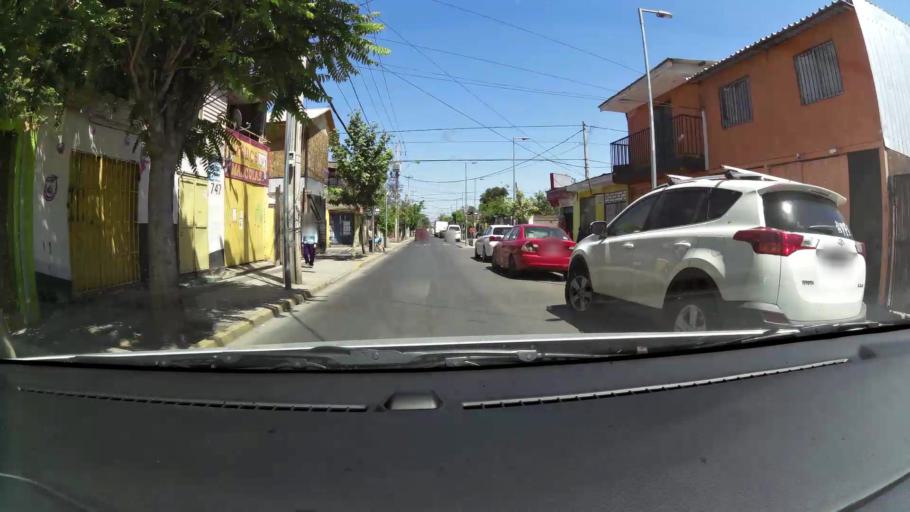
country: CL
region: Santiago Metropolitan
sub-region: Provincia de Maipo
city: San Bernardo
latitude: -33.5660
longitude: -70.6751
